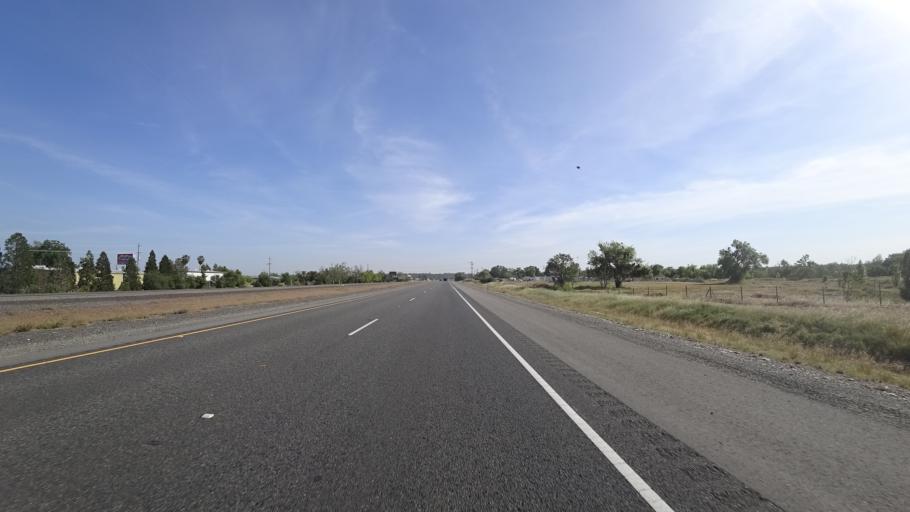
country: US
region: California
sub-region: Butte County
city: South Oroville
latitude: 39.4852
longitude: -121.5757
